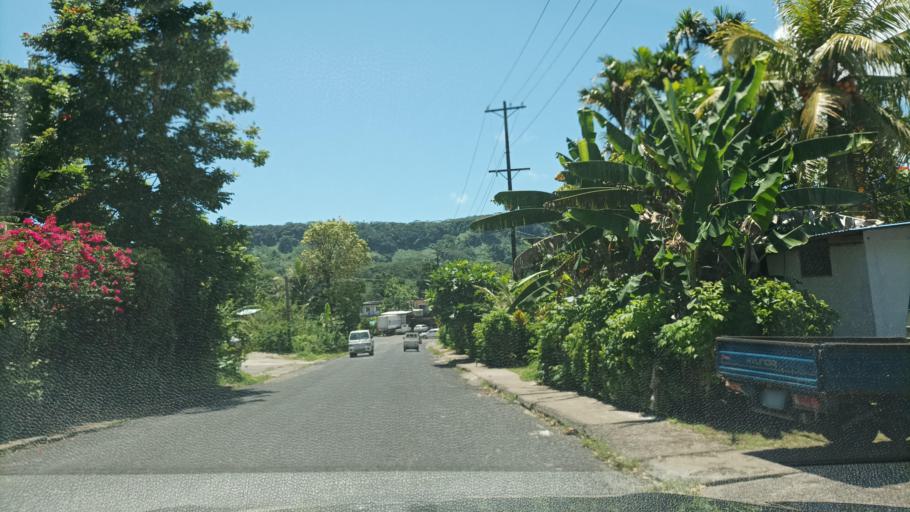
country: FM
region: Pohnpei
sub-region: Kolonia Municipality
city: Kolonia
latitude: 6.9613
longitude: 158.2140
